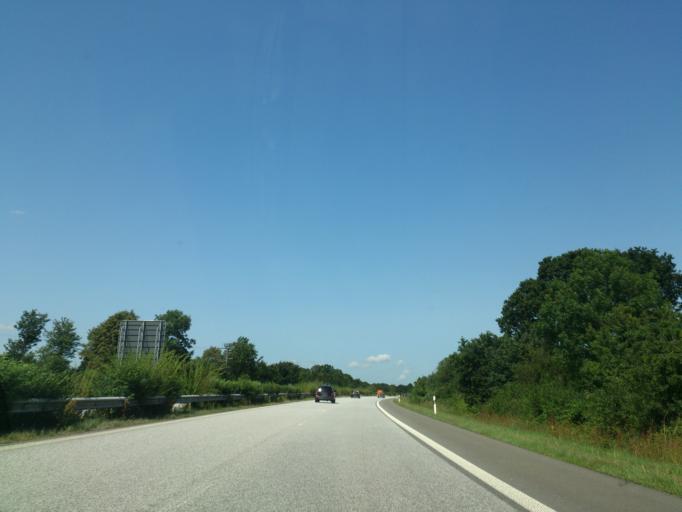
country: DE
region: Schleswig-Holstein
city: Schafstedt
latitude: 54.0780
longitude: 9.2754
